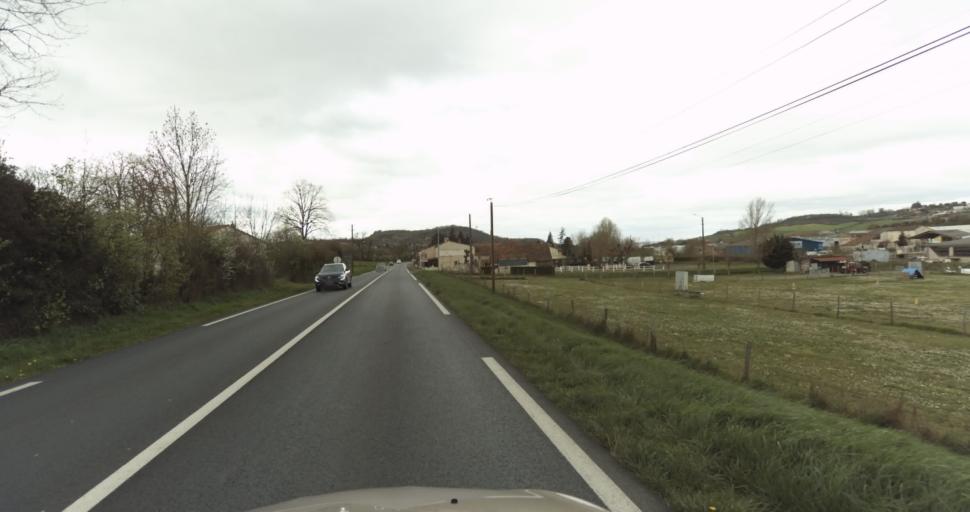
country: FR
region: Midi-Pyrenees
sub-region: Departement du Tarn
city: Puygouzon
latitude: 43.8903
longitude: 2.1609
